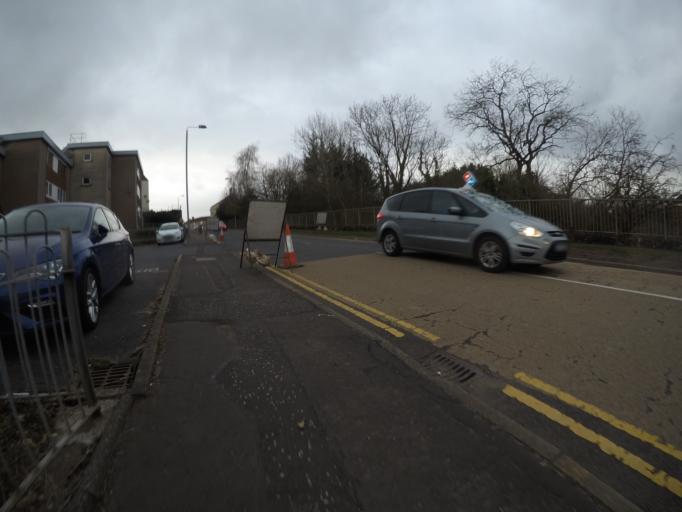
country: GB
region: Scotland
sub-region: East Ayrshire
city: Kilmarnock
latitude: 55.6146
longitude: -4.4931
